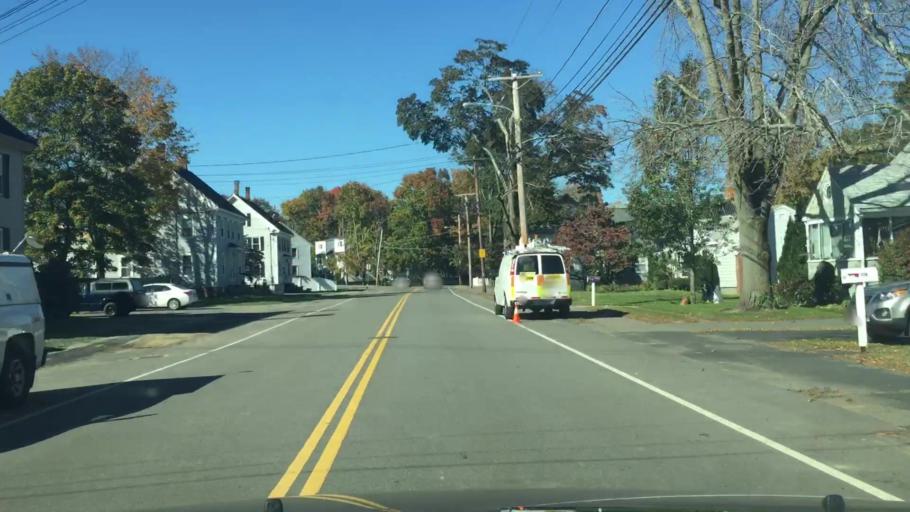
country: US
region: Massachusetts
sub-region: Essex County
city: North Andover
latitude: 42.6974
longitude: -71.1216
